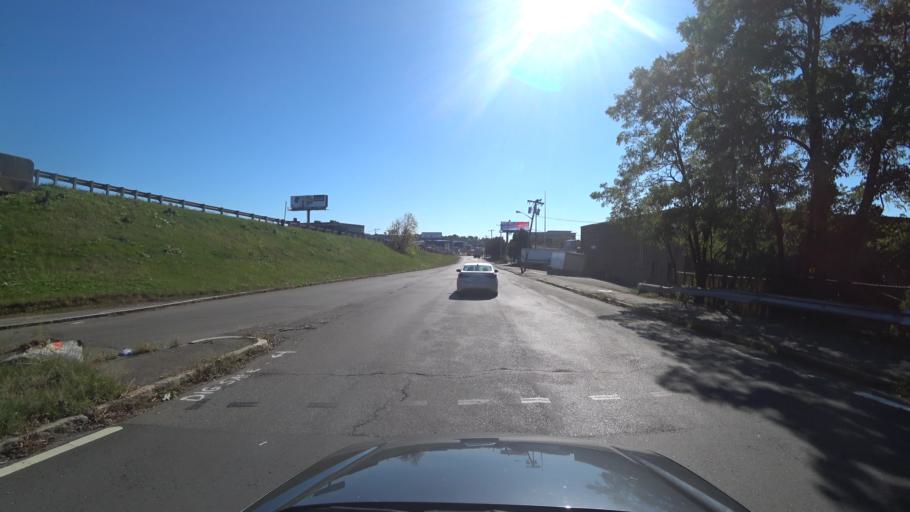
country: US
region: Massachusetts
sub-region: Suffolk County
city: Revere
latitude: 42.4043
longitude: -71.0033
